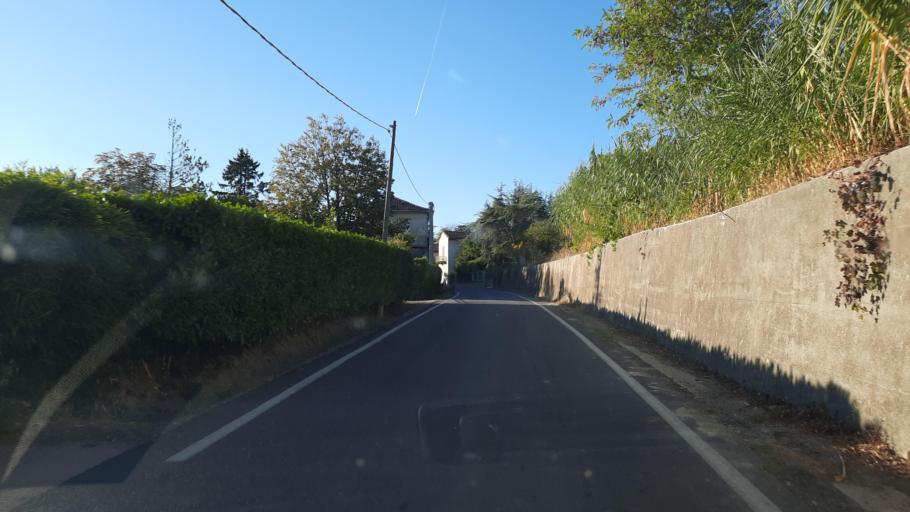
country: IT
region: Piedmont
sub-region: Provincia di Alessandria
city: Vignale Monferrato
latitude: 45.0067
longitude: 8.4093
